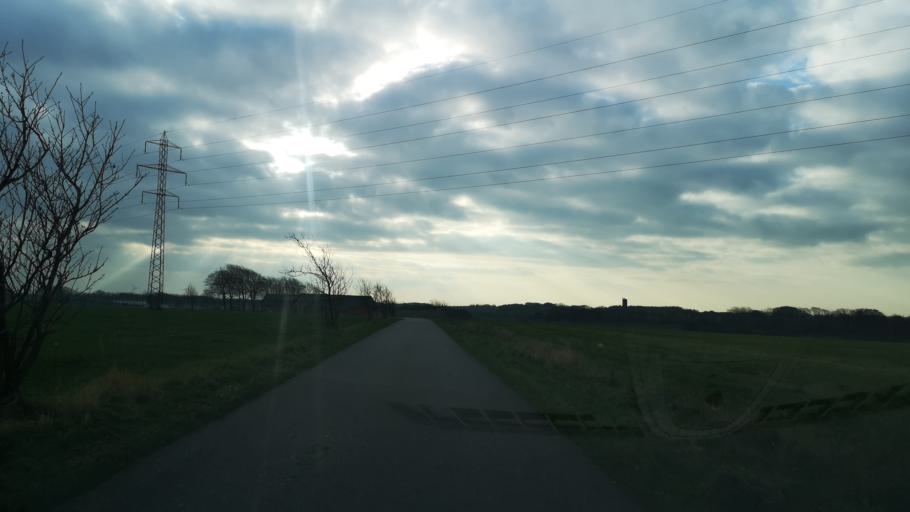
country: DK
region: Central Jutland
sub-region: Ringkobing-Skjern Kommune
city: Videbaek
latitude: 56.0005
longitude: 8.5887
